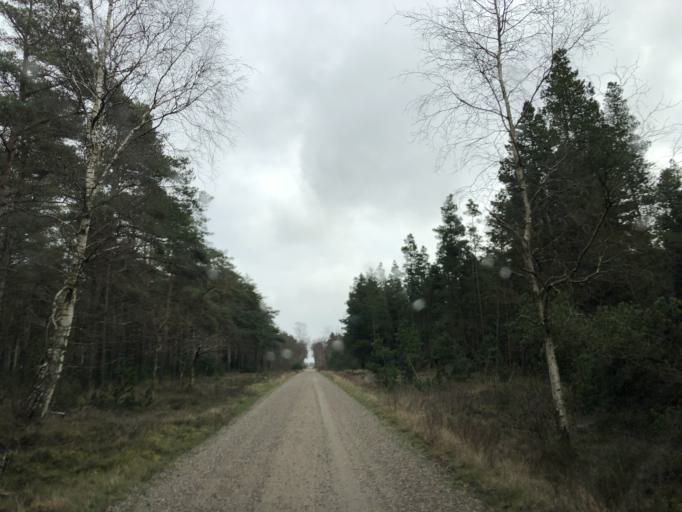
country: DK
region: Central Jutland
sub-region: Holstebro Kommune
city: Ulfborg
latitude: 56.2954
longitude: 8.1825
